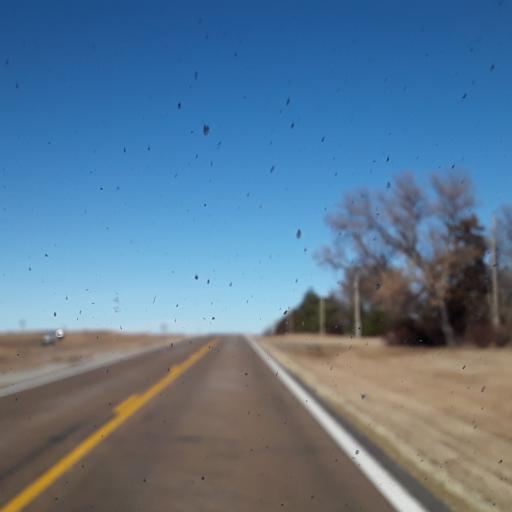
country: US
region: Kansas
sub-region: Mitchell County
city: Beloit
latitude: 39.3171
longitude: -98.1163
